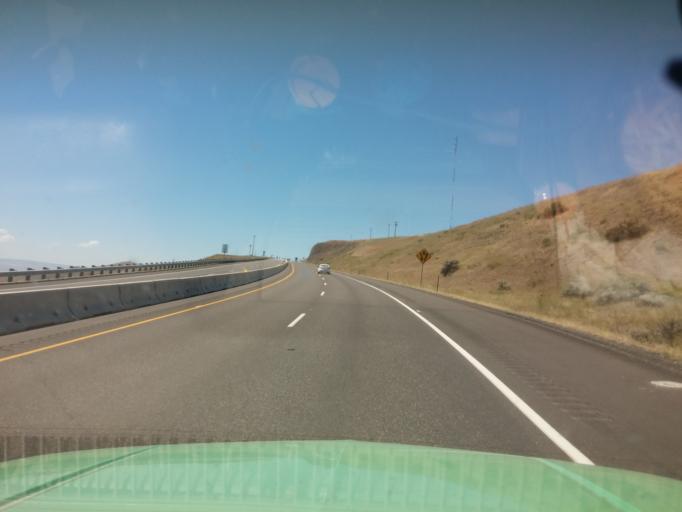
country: US
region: Idaho
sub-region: Nez Perce County
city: Lewiston
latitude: 46.4627
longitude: -116.9968
